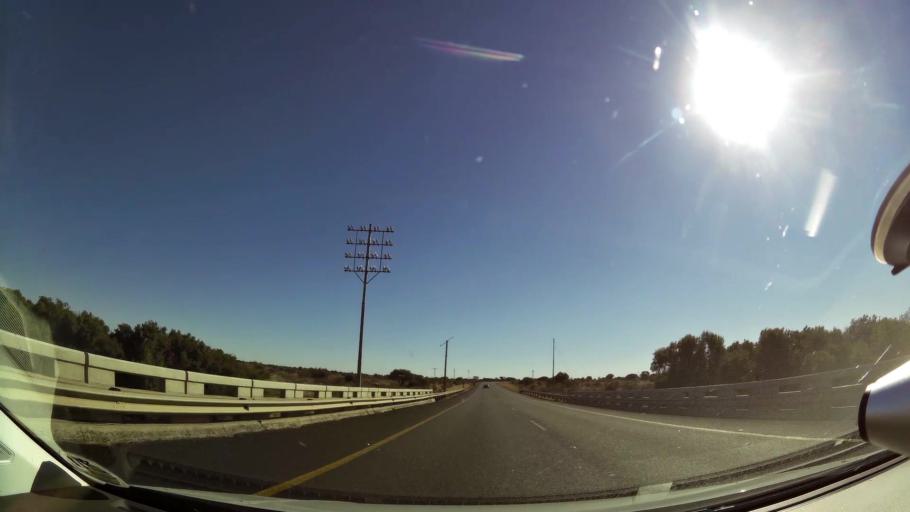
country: ZA
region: Northern Cape
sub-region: Frances Baard District Municipality
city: Warrenton
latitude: -28.0948
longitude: 24.8678
